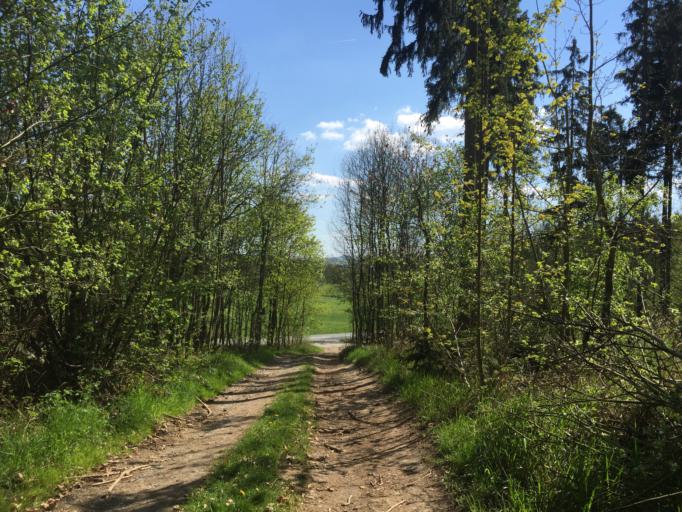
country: DE
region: Saxony
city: Neuensalz
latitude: 50.5017
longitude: 12.1863
